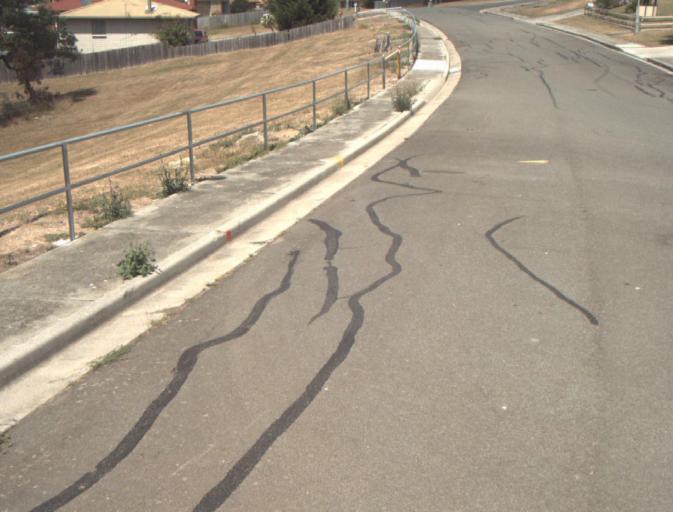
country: AU
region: Tasmania
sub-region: Launceston
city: Newstead
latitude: -41.4083
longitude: 147.1701
